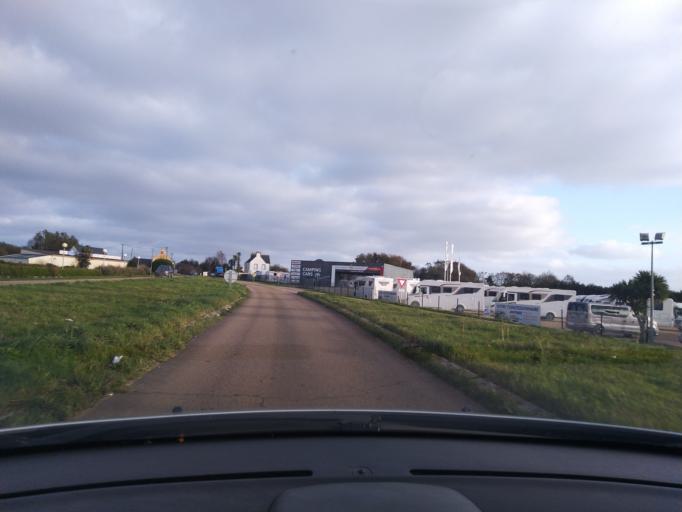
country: FR
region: Brittany
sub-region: Departement du Finistere
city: Morlaix
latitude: 48.5788
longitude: -3.7963
